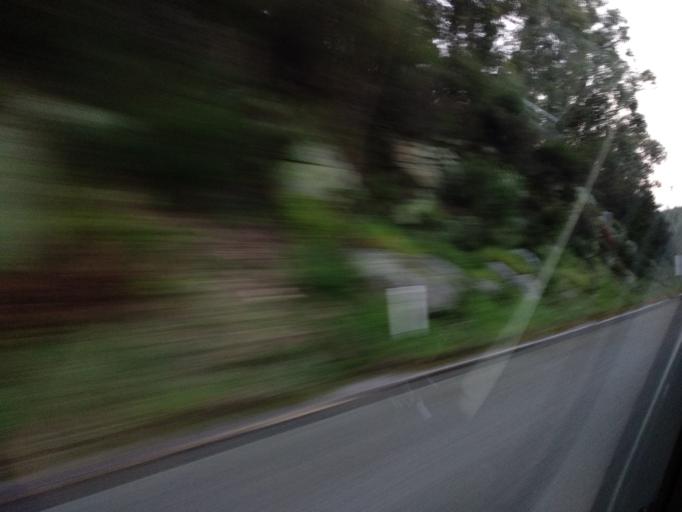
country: PT
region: Braga
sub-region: Braga
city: Oliveira
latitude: 41.4568
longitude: -8.4830
